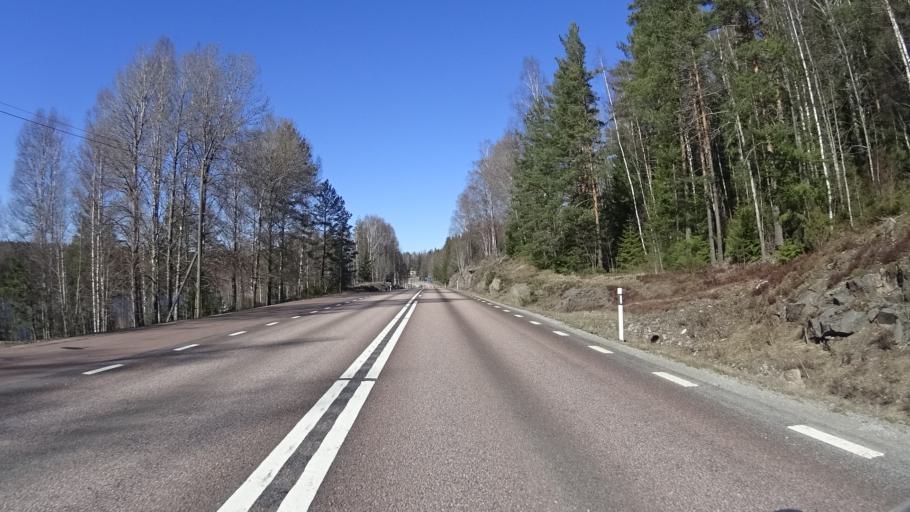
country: SE
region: Vaermland
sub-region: Sunne Kommun
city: Sunne
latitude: 59.6467
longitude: 12.9447
